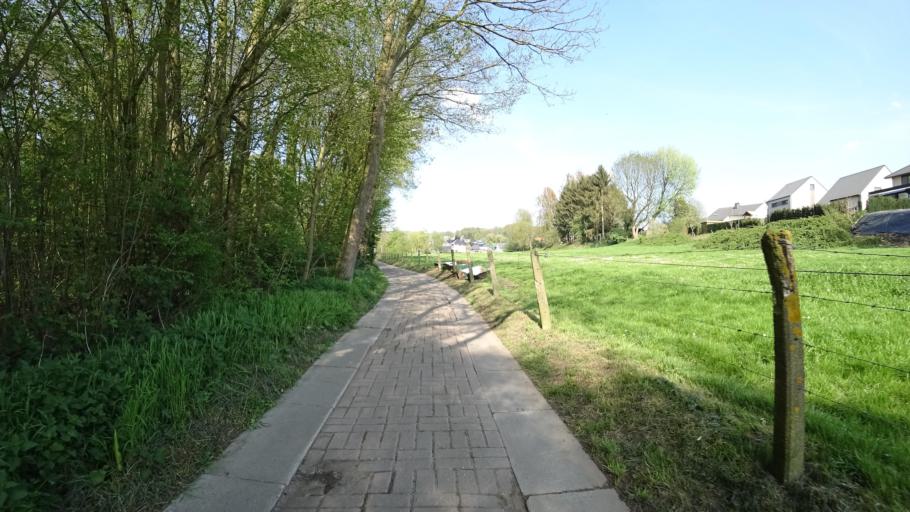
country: BE
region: Flanders
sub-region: Provincie Vlaams-Brabant
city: Beersel
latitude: 50.7296
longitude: 4.2929
